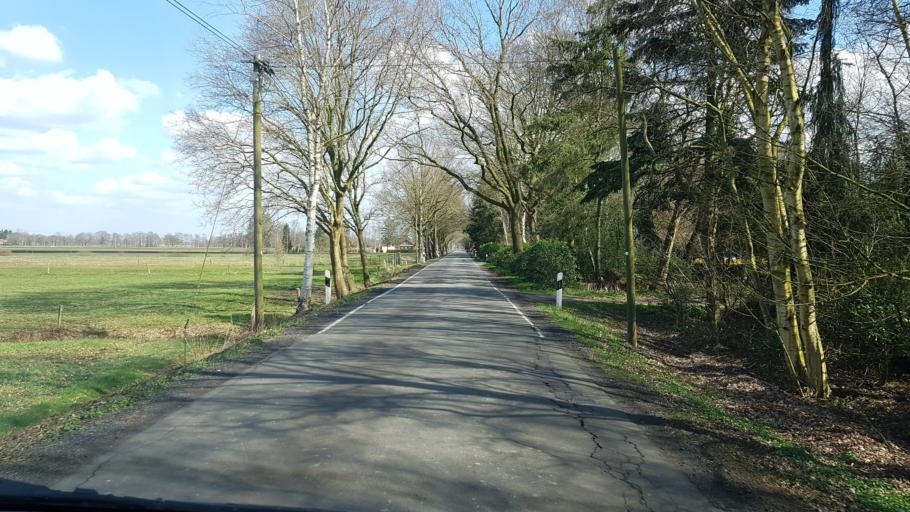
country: DE
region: Lower Saxony
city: Rastede
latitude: 53.2984
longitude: 8.2013
